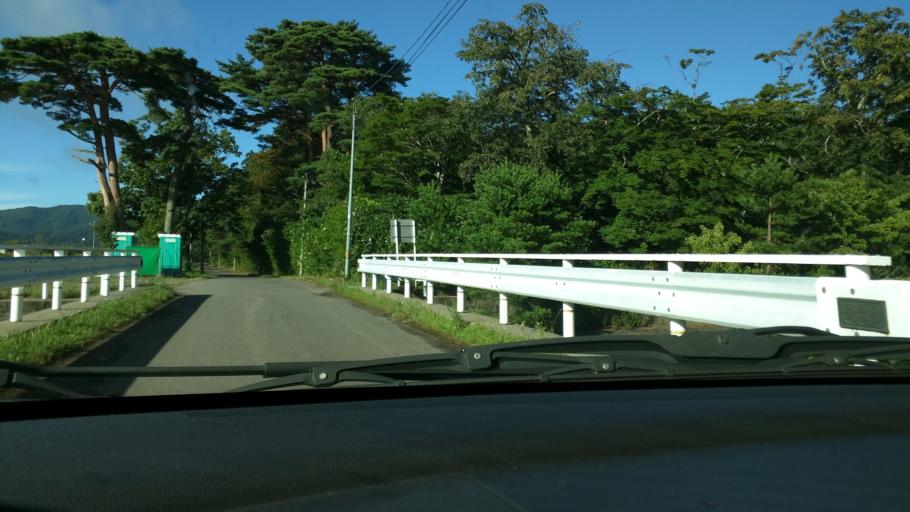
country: JP
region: Fukushima
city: Inawashiro
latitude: 37.4262
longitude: 140.1371
